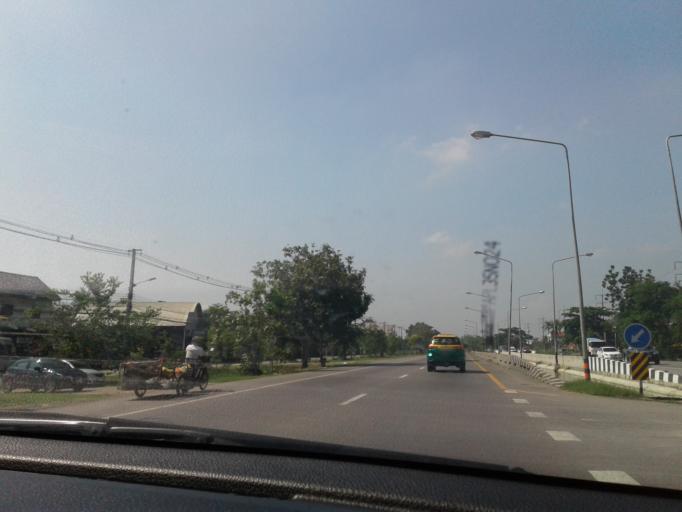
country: TH
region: Ratchaburi
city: Bang Phae
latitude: 13.7370
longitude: 99.9138
